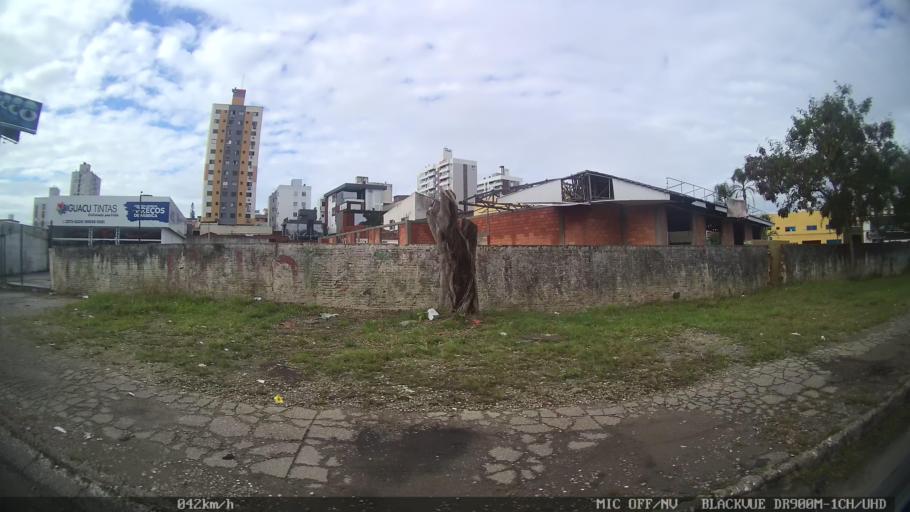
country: BR
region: Santa Catarina
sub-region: Sao Jose
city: Campinas
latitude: -27.5716
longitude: -48.6135
